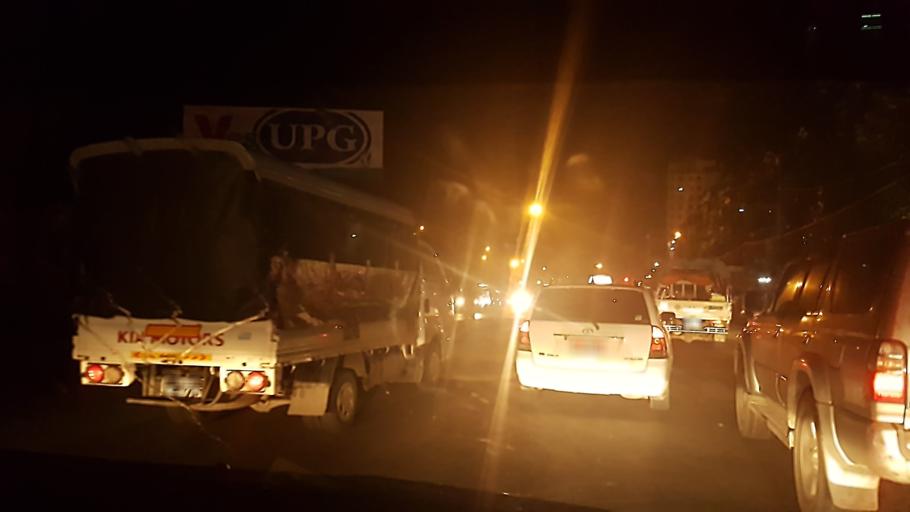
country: MM
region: Yangon
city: Yangon
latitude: 16.7721
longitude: 96.1518
